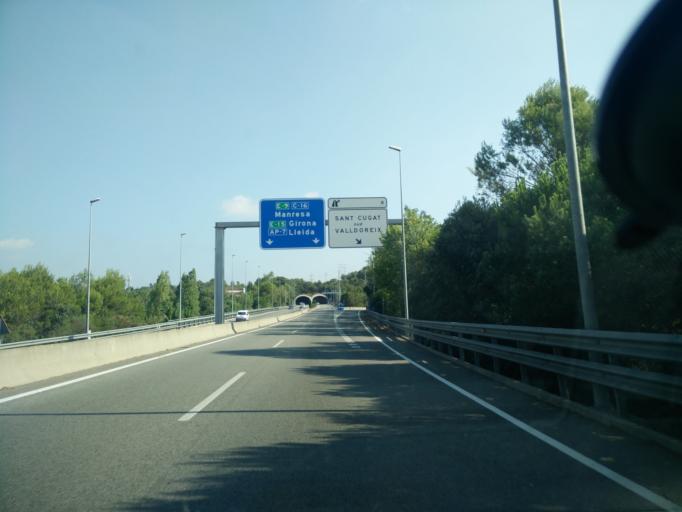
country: ES
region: Catalonia
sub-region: Provincia de Barcelona
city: Sant Cugat del Valles
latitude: 41.4470
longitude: 2.0694
